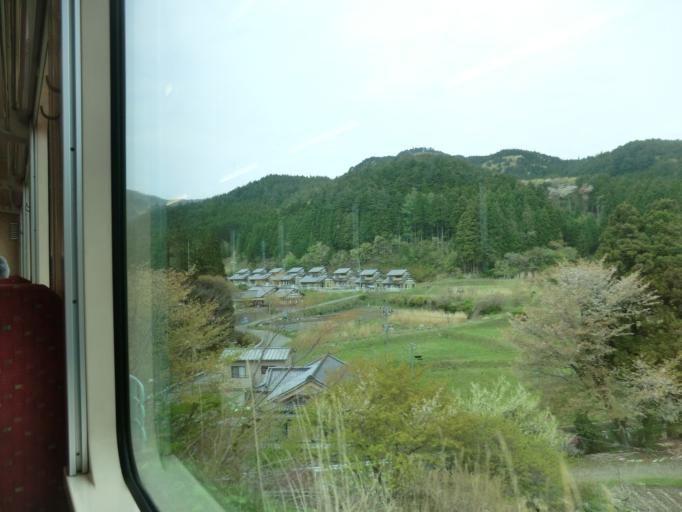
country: JP
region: Iwate
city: Ofunato
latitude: 39.0548
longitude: 141.7891
